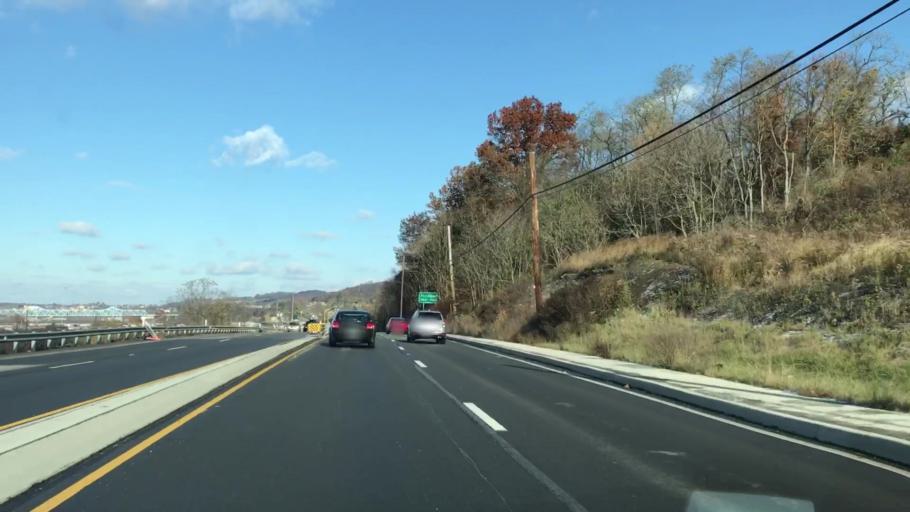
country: US
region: Pennsylvania
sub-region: Beaver County
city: Freedom
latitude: 40.6731
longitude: -80.2459
